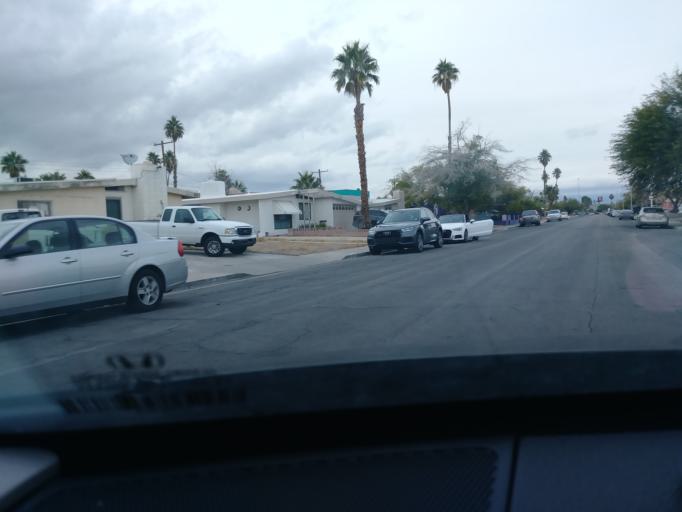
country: US
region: Nevada
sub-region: Clark County
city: Spring Valley
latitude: 36.1684
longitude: -115.2229
